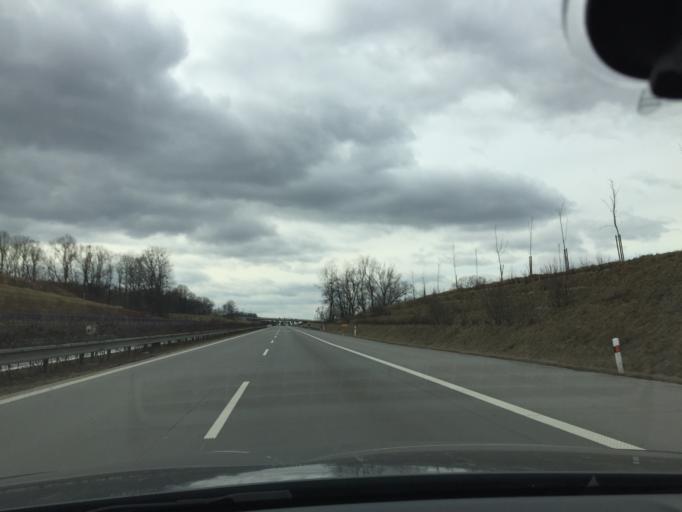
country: CZ
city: Staric
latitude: 49.6608
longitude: 18.2665
